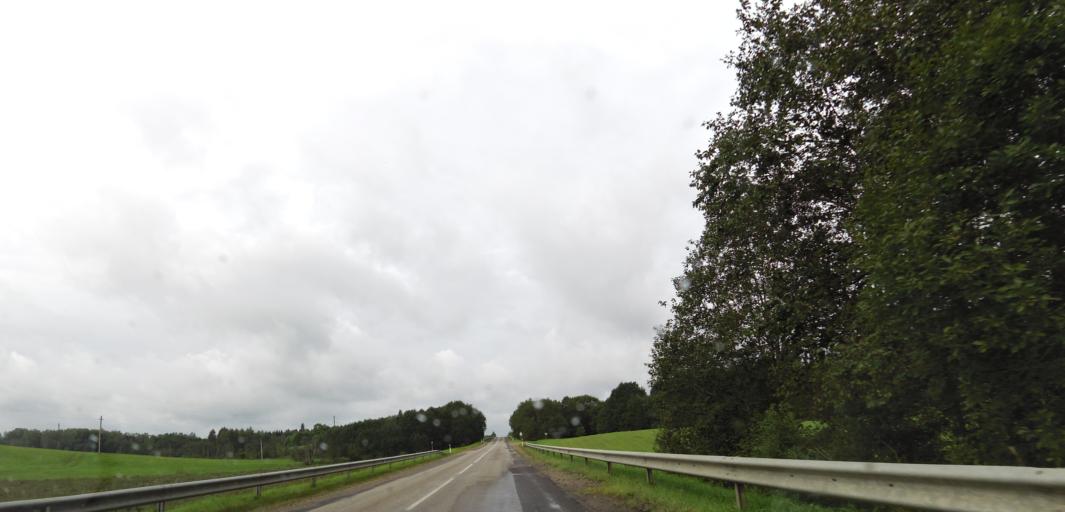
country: LT
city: Moletai
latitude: 55.2119
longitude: 25.3046
